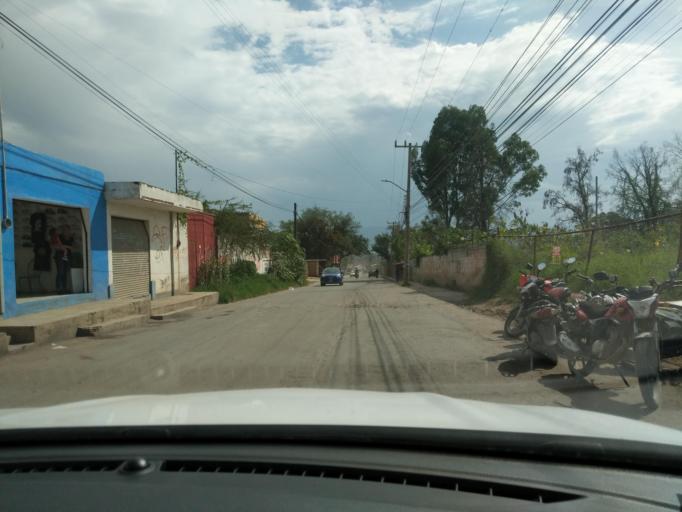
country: MX
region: Jalisco
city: San Jose del Castillo
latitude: 20.5167
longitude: -103.2355
